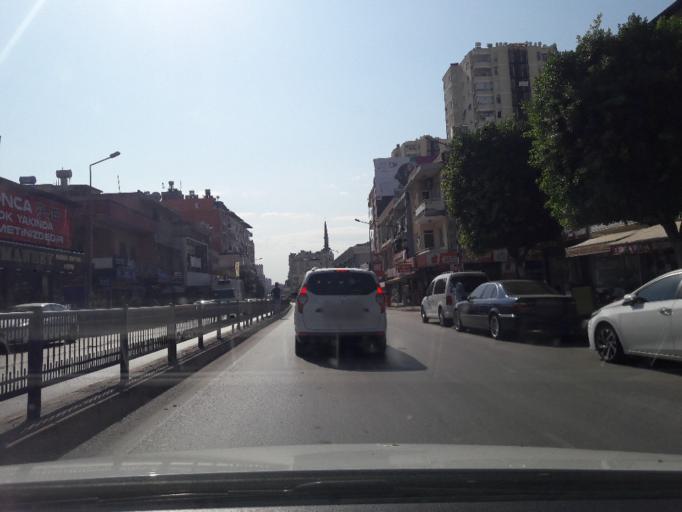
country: TR
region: Adana
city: Adana
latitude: 37.0140
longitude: 35.3224
